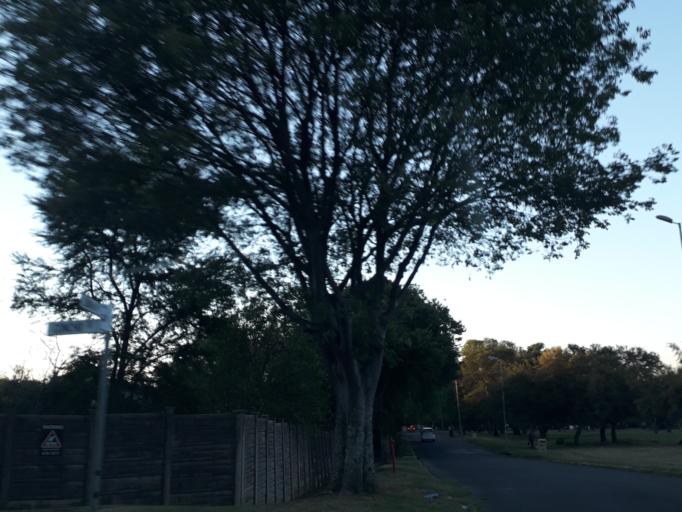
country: ZA
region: Gauteng
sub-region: City of Johannesburg Metropolitan Municipality
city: Roodepoort
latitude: -26.1330
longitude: 27.9562
